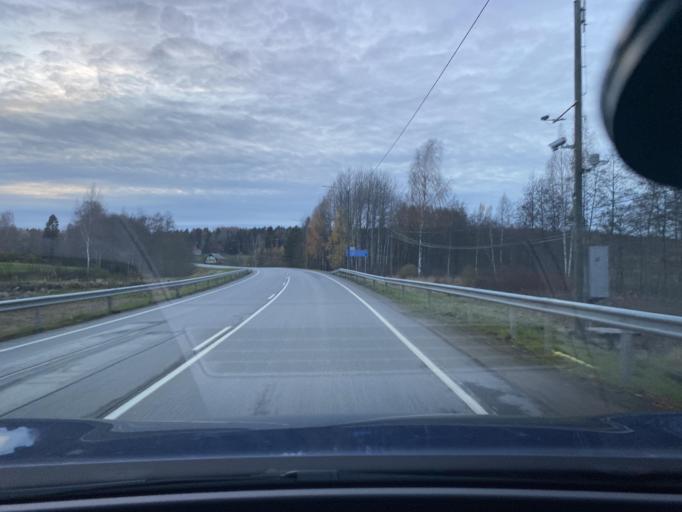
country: FI
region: Uusimaa
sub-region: Helsinki
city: Saukkola
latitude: 60.3897
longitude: 24.0331
